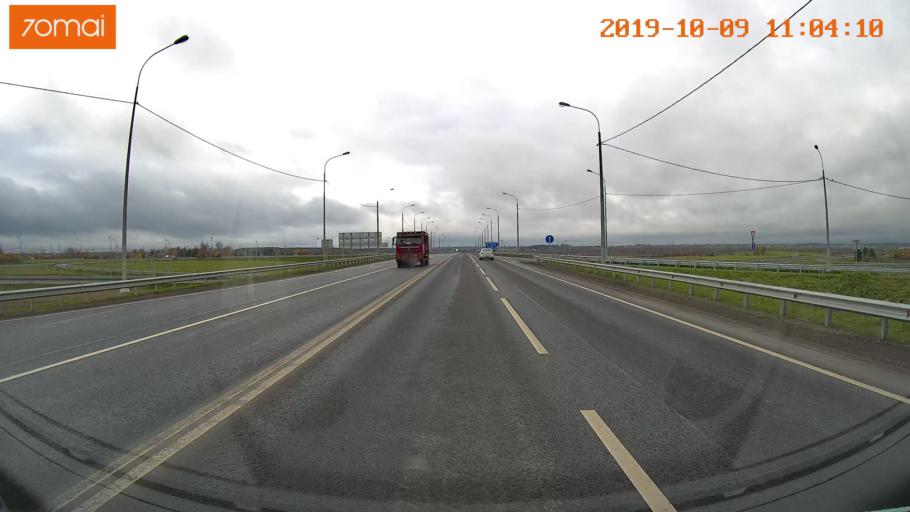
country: RU
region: Vologda
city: Vologda
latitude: 59.2149
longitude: 39.7703
